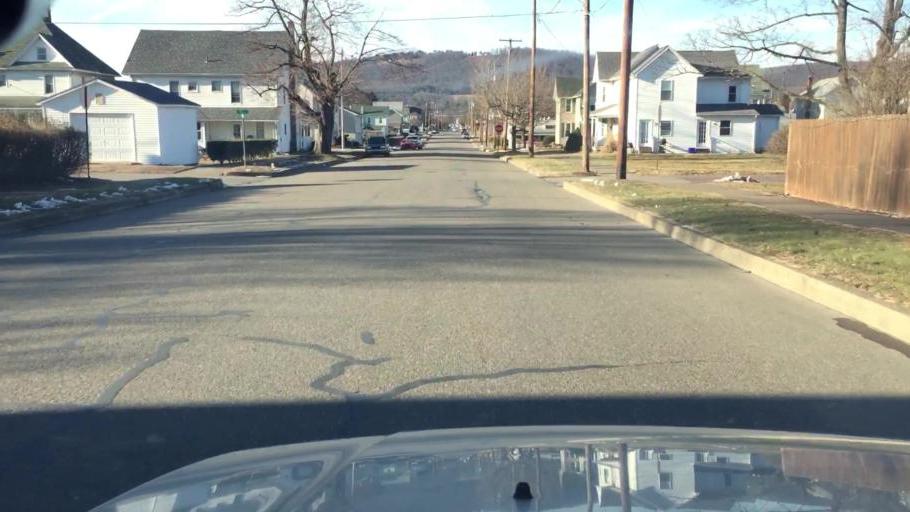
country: US
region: Pennsylvania
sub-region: Columbia County
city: Berwick
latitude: 41.0611
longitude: -76.2317
